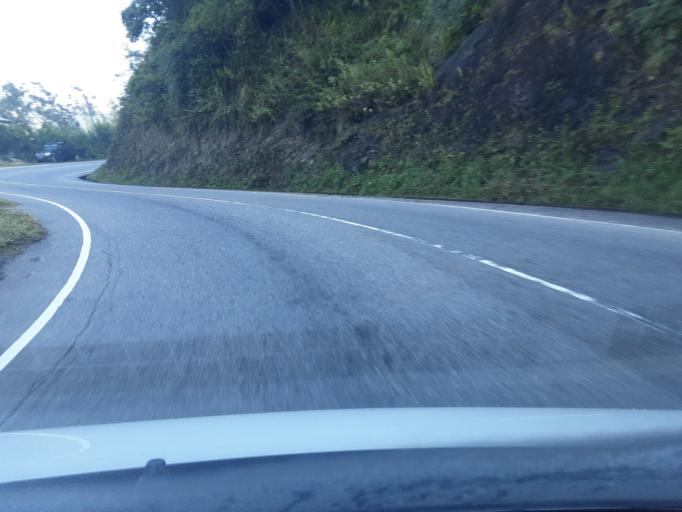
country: LK
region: Uva
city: Badulla
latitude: 6.9235
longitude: 80.9651
